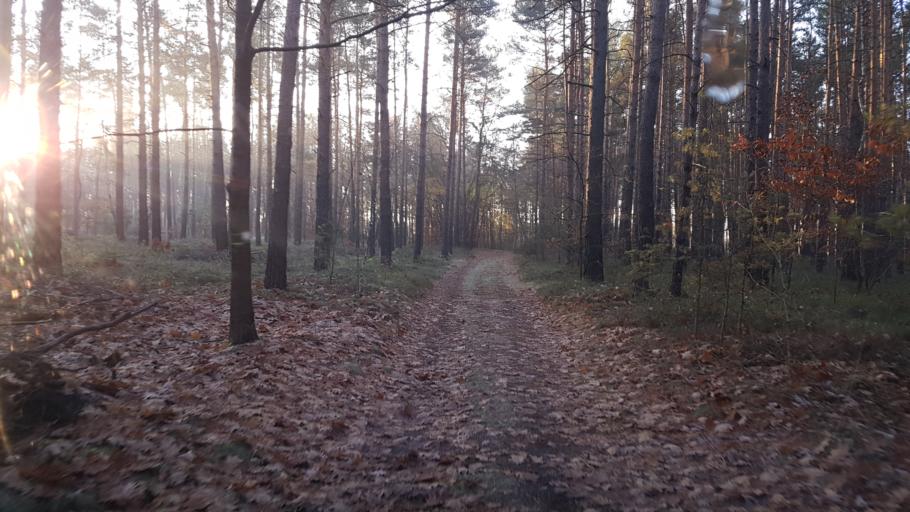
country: DE
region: Brandenburg
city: Sallgast
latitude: 51.6029
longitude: 13.8351
